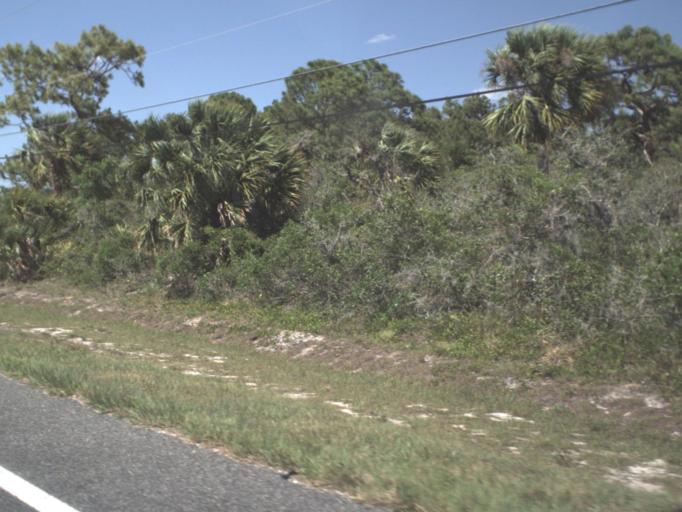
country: US
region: Florida
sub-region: Volusia County
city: Oak Hill
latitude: 28.7701
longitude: -80.8786
